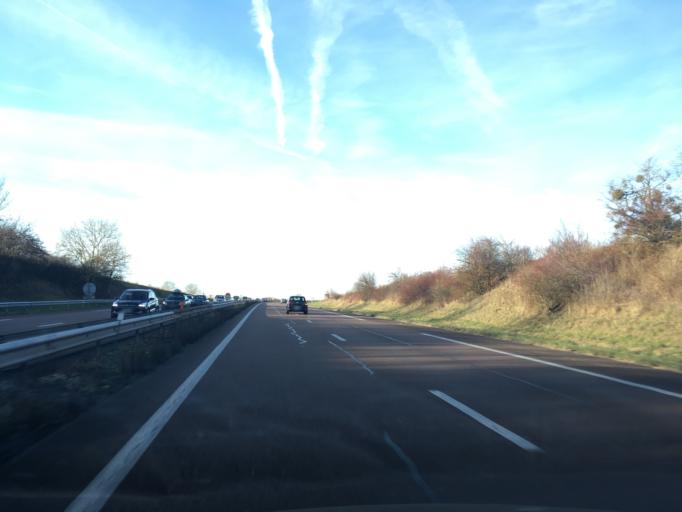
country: FR
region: Bourgogne
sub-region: Departement de l'Yonne
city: Avallon
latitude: 47.5597
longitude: 3.9470
